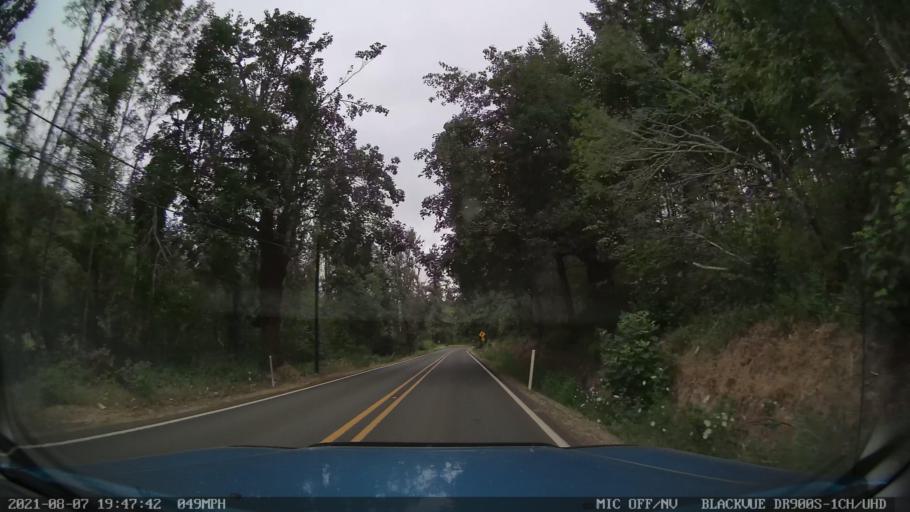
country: US
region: Oregon
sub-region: Marion County
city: Silverton
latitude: 44.9666
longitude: -122.7115
